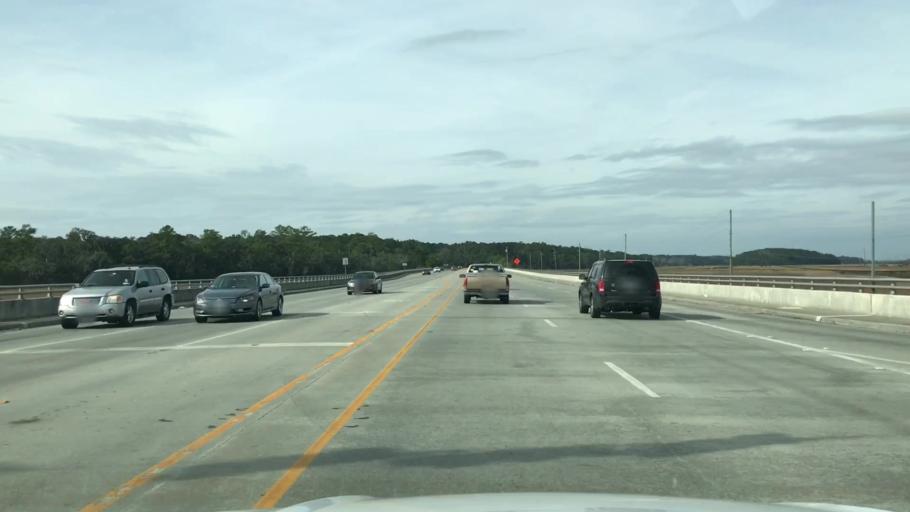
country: US
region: South Carolina
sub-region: Charleston County
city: Shell Point
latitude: 32.7515
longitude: -80.0230
